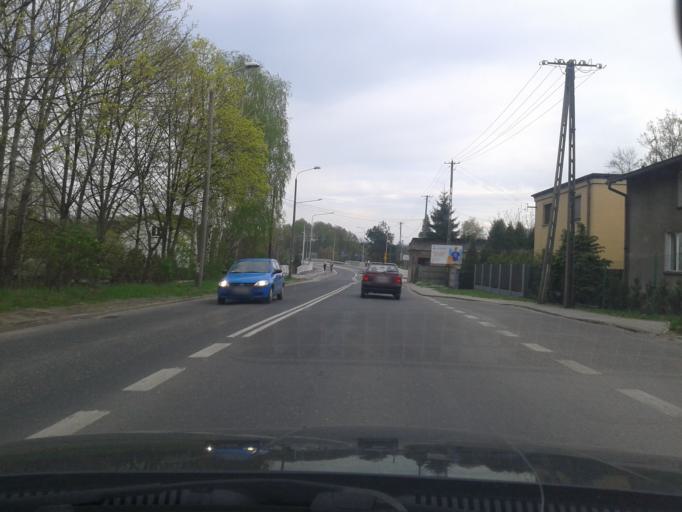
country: PL
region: Silesian Voivodeship
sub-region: Rybnik
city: Rybnik
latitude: 50.1162
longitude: 18.5274
